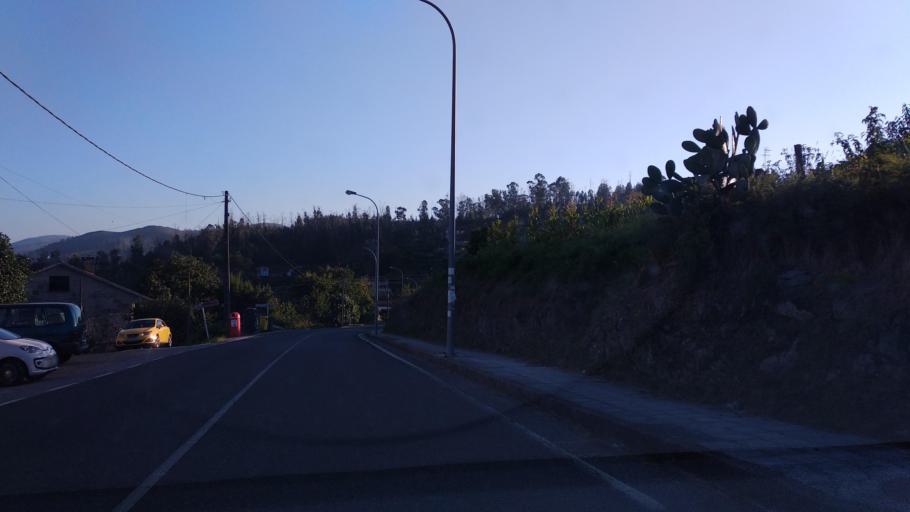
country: ES
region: Galicia
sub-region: Provincia de Pontevedra
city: Ponte Caldelas
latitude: 42.3532
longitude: -8.5430
